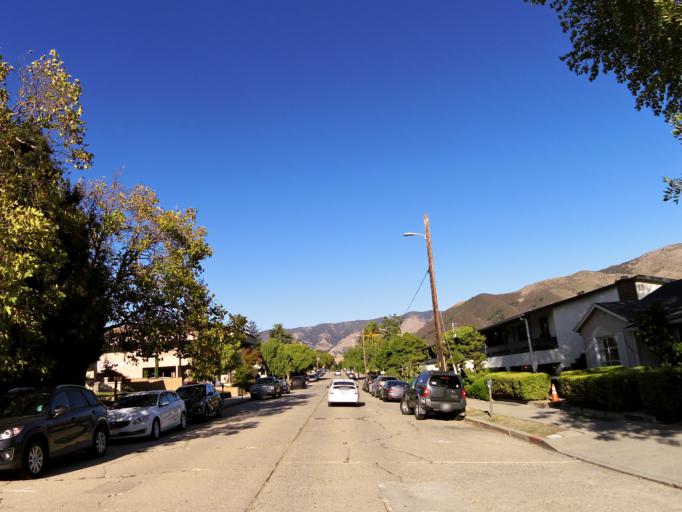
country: US
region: California
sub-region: San Luis Obispo County
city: San Luis Obispo
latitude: 35.2837
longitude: -120.6603
